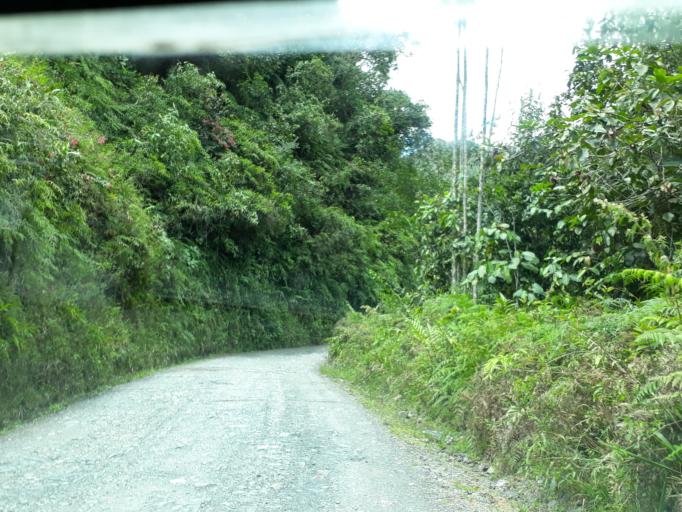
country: CO
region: Cundinamarca
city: Topaipi
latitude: 5.3459
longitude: -74.1946
